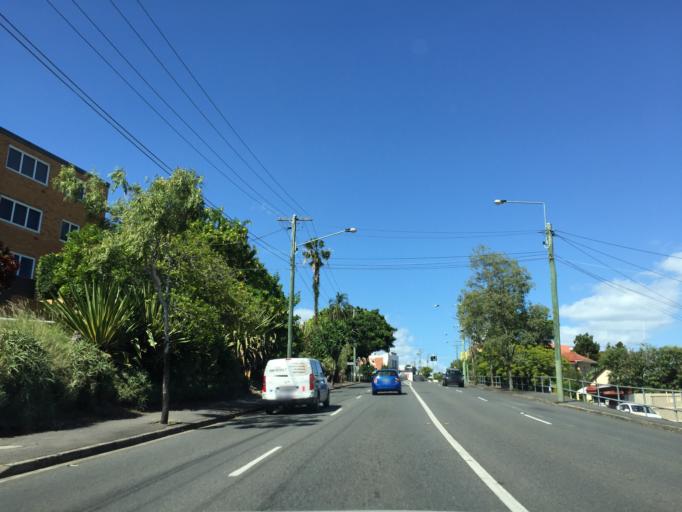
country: AU
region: Queensland
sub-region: Brisbane
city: Milton
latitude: -27.4535
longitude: 153.0060
